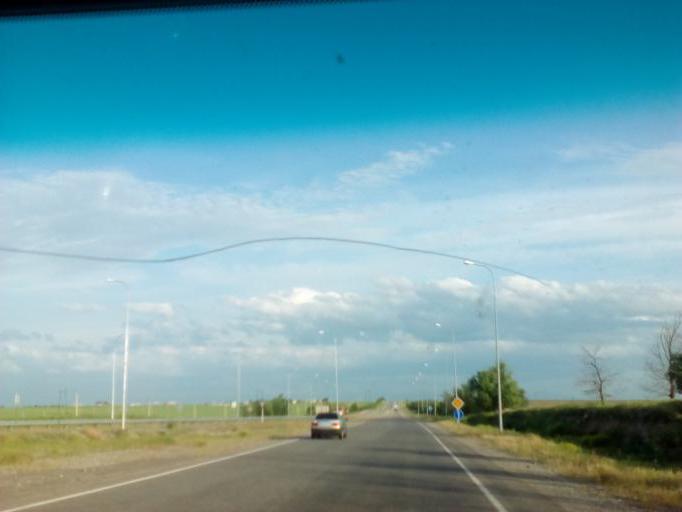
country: KZ
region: Ongtustik Qazaqstan
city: Temirlanovka
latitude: 42.5260
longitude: 69.3433
